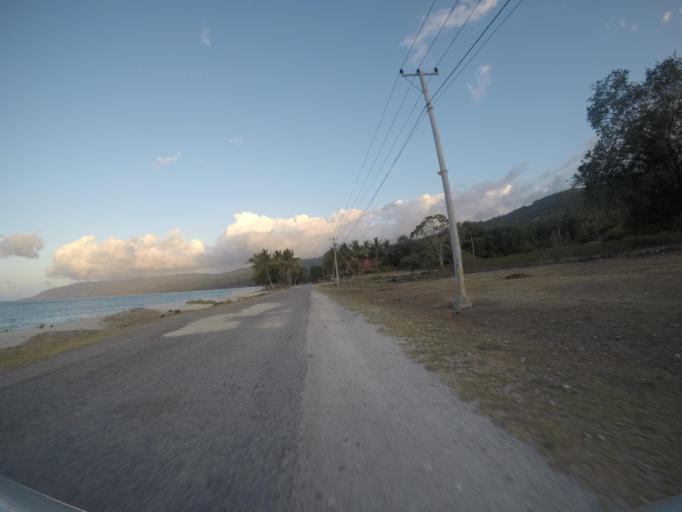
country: TL
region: Lautem
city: Lospalos
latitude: -8.3551
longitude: 127.0561
